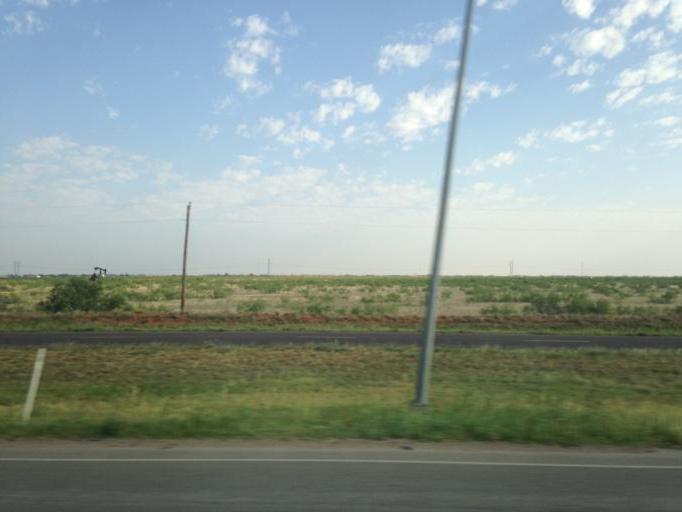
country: US
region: Texas
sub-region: Midland County
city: Midland
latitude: 32.0524
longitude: -101.9661
